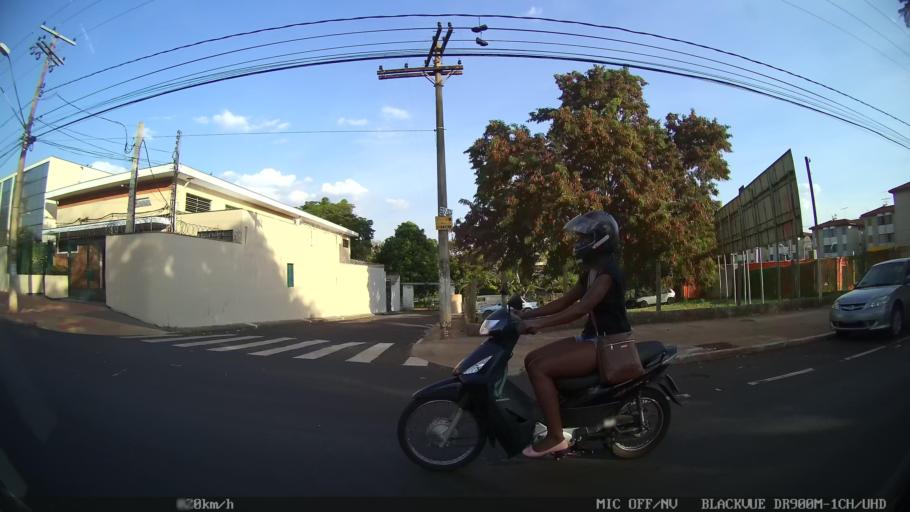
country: BR
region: Sao Paulo
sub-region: Ribeirao Preto
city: Ribeirao Preto
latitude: -21.1749
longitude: -47.8333
